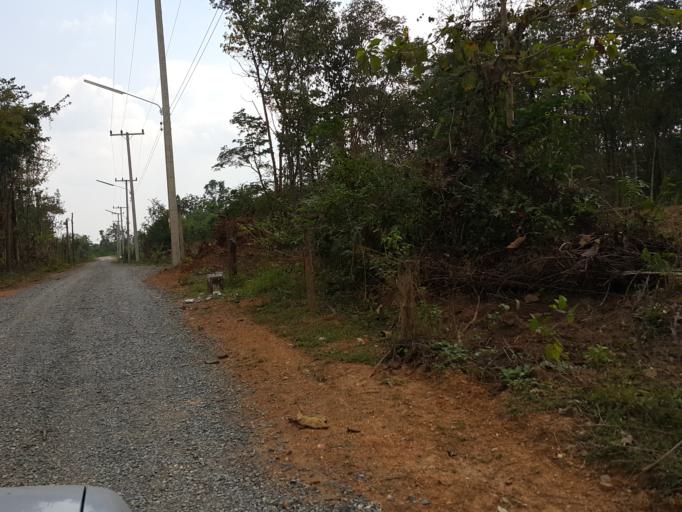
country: TH
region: Sukhothai
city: Thung Saliam
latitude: 17.3501
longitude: 99.5866
